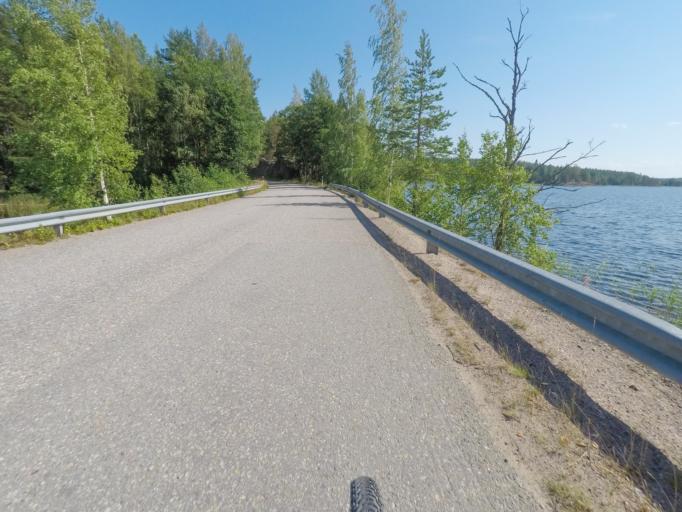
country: FI
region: Southern Savonia
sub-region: Mikkeli
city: Puumala
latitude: 61.4199
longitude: 28.1147
